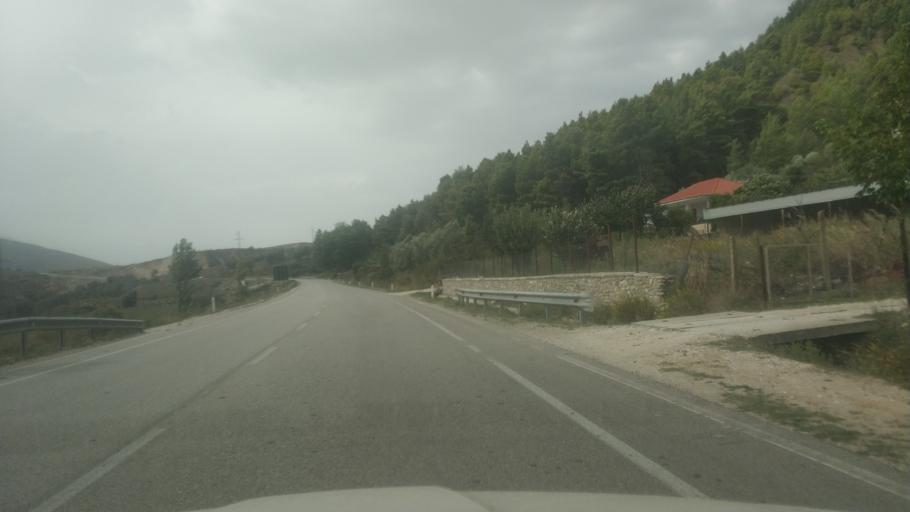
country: AL
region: Gjirokaster
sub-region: Rrethi i Tepelenes
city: Memaliaj
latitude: 40.3546
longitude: 19.9490
